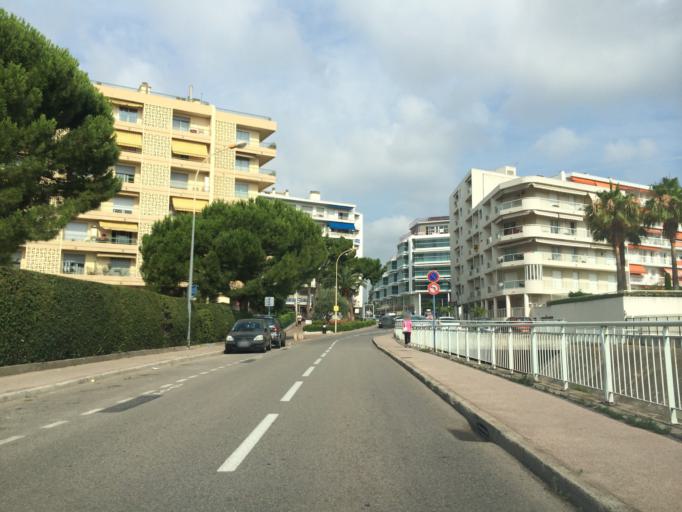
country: FR
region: Provence-Alpes-Cote d'Azur
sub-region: Departement des Alpes-Maritimes
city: Cagnes-sur-Mer
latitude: 43.6572
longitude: 7.1522
